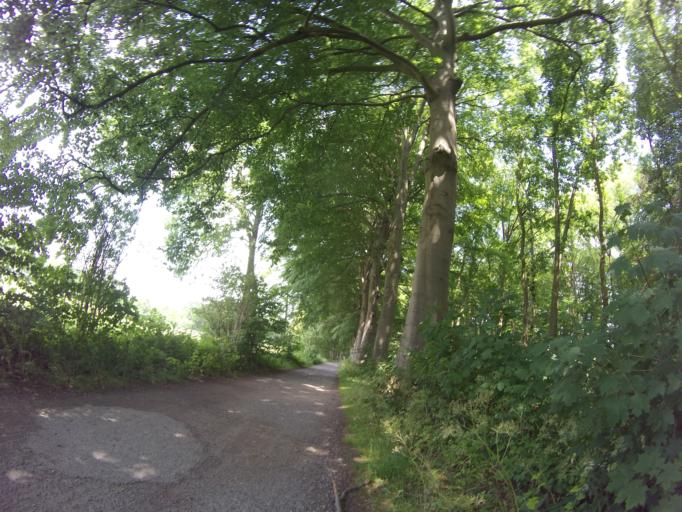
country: NL
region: Utrecht
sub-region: Gemeente De Bilt
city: De Bilt
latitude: 52.1270
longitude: 5.1561
